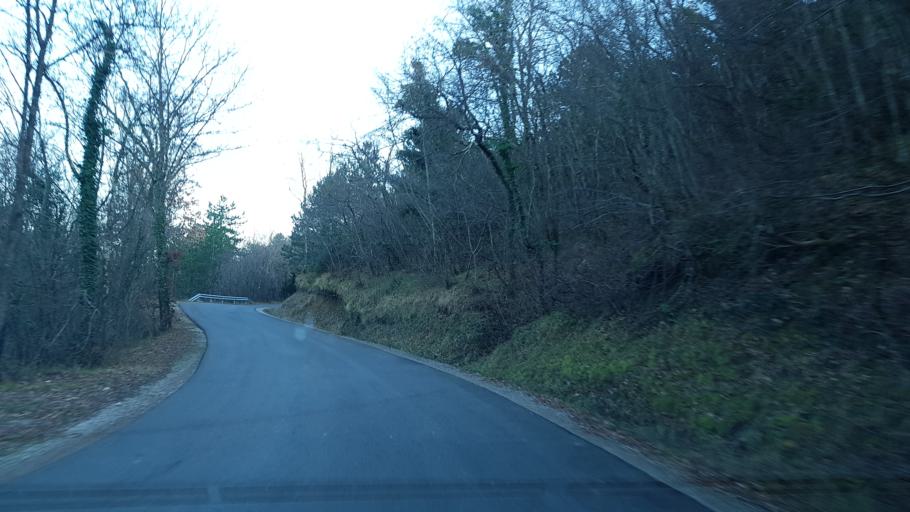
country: SI
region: Koper-Capodistria
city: Pobegi
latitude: 45.4935
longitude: 13.7880
